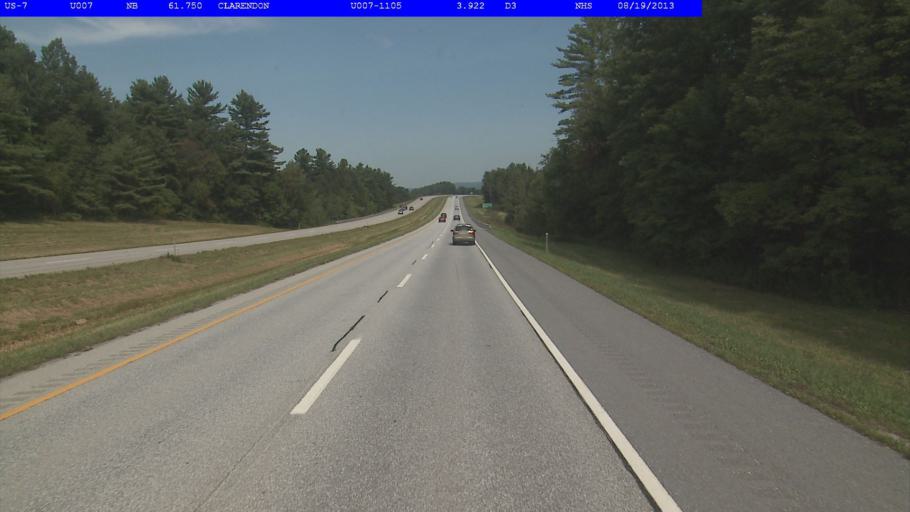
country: US
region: Vermont
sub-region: Rutland County
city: Rutland
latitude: 43.5481
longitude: -72.9613
